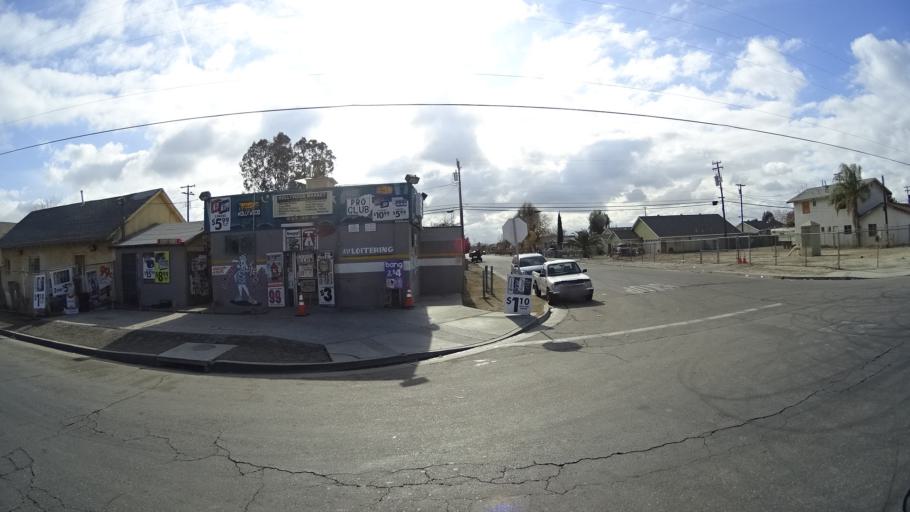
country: US
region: California
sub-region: Kern County
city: Bakersfield
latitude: 35.3250
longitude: -118.9920
